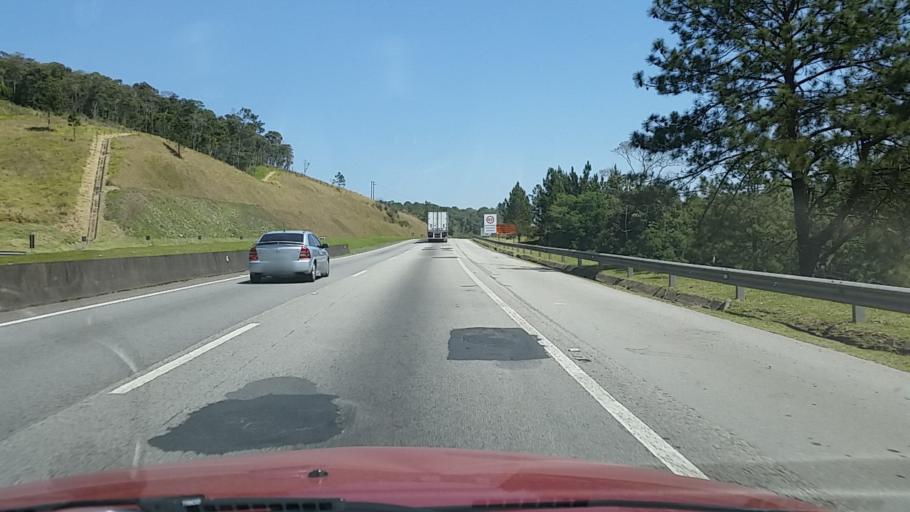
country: BR
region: Sao Paulo
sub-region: Juquitiba
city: Juquitiba
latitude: -23.9728
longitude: -47.1369
